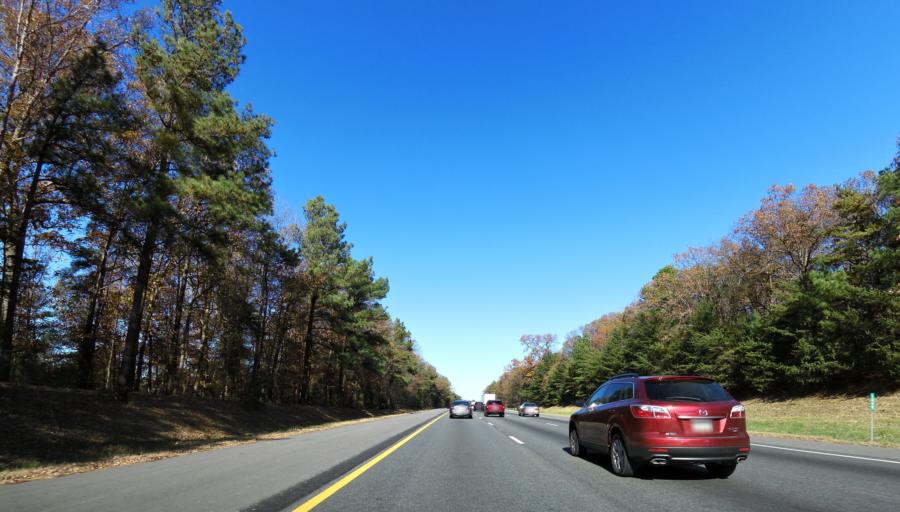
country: US
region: Virginia
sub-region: Caroline County
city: Bowling Green
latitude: 38.0089
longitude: -77.4974
